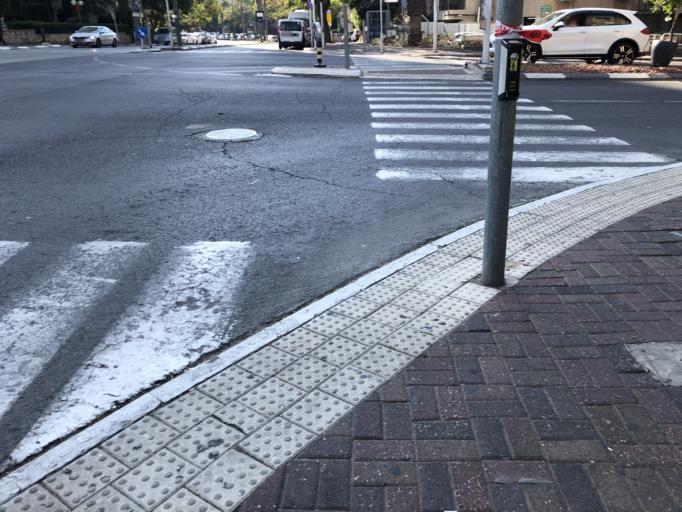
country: IL
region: Tel Aviv
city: Giv`atayim
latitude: 32.0667
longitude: 34.8085
